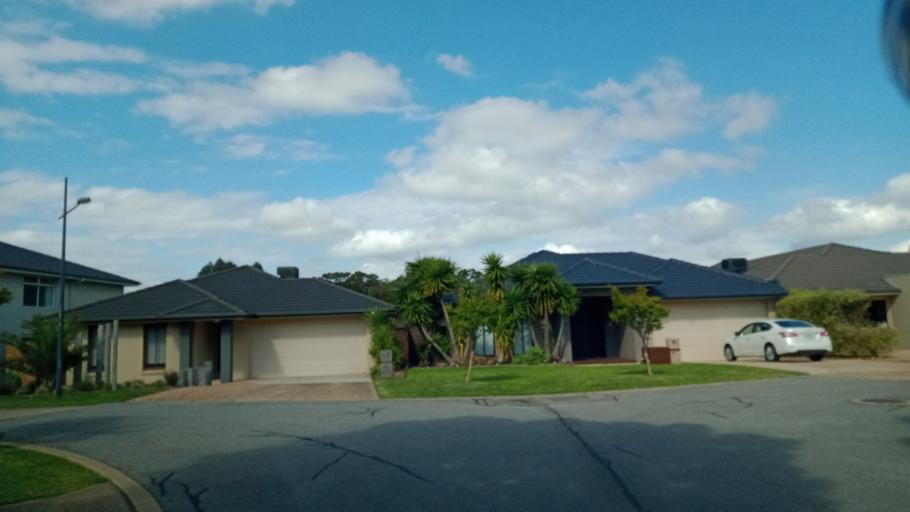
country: AU
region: Victoria
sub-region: Frankston
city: Sandhurst
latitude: -38.0887
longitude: 145.2165
